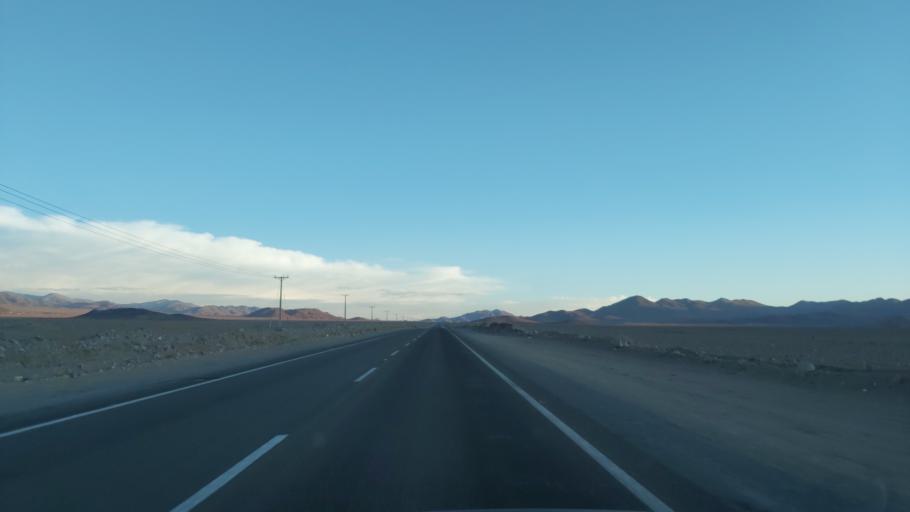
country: CL
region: Atacama
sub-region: Provincia de Chanaral
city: Diego de Almagro
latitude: -26.7004
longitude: -69.9267
